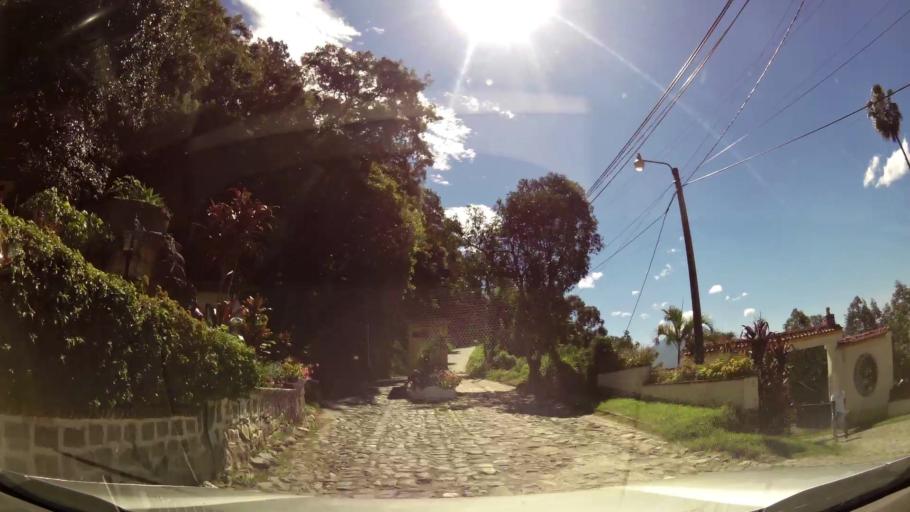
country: GT
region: Solola
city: Panajachel
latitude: 14.7473
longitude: -91.1635
